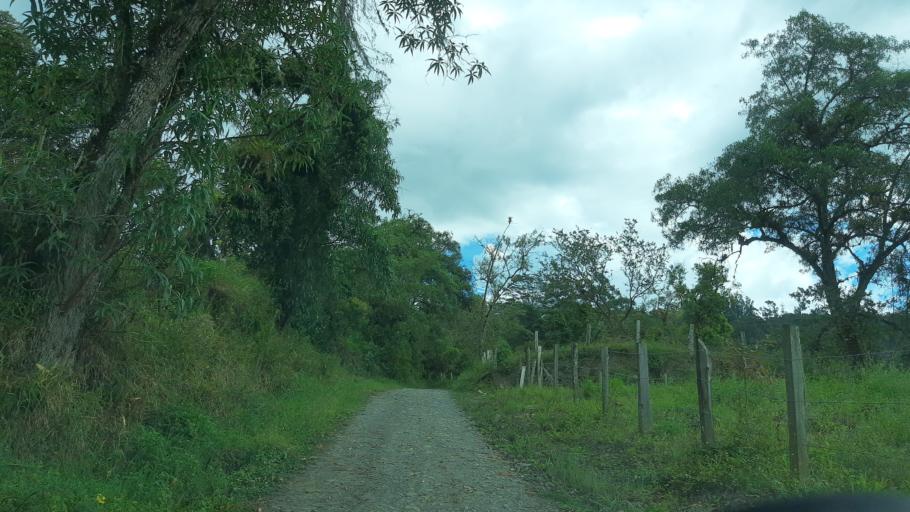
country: CO
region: Boyaca
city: Garagoa
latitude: 5.0393
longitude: -73.3316
